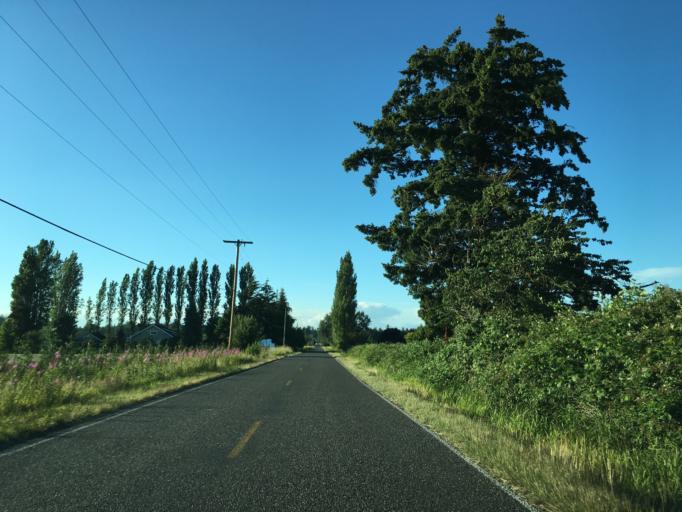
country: US
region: Washington
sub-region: Whatcom County
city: Lynden
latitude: 48.9671
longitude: -122.5301
